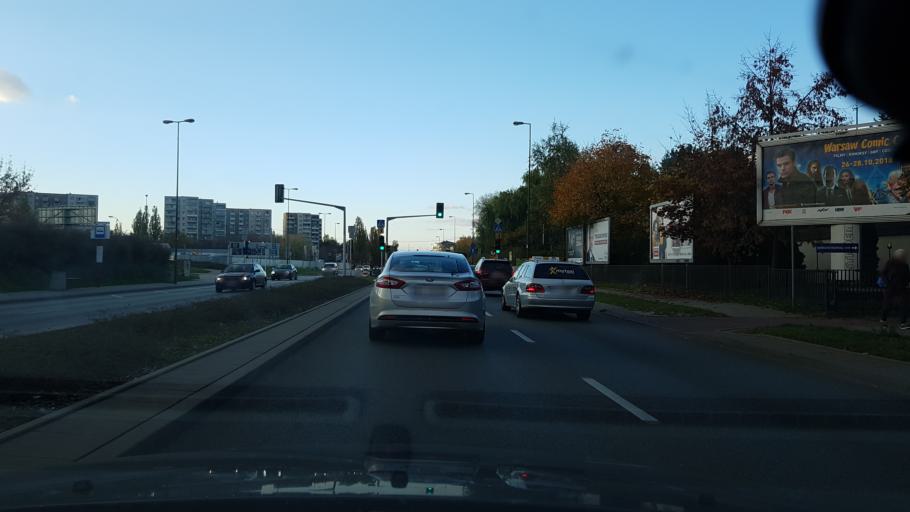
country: PL
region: Masovian Voivodeship
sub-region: Warszawa
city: Ursynow
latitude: 52.1475
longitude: 21.0615
